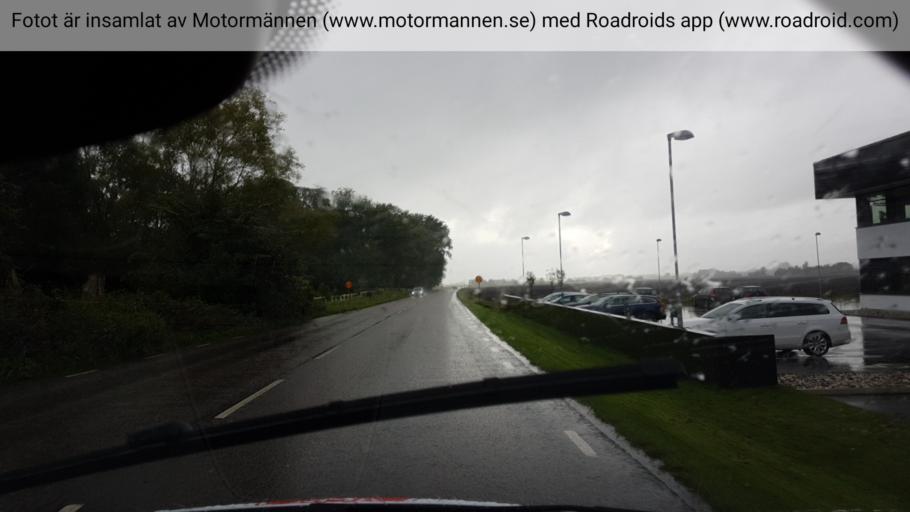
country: SE
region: Halland
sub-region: Laholms Kommun
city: Laholm
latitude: 56.4652
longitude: 13.0196
